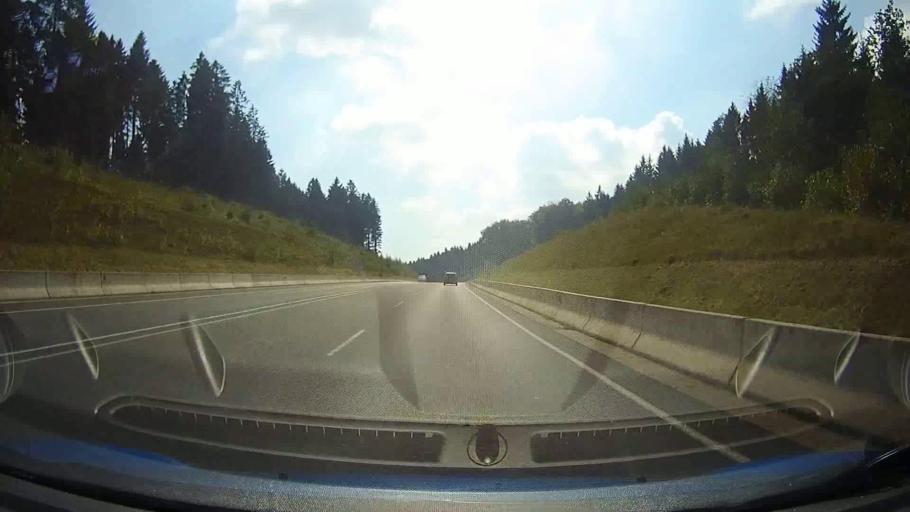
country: DE
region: Lower Saxony
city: Adelebsen
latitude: 51.6419
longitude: 9.7646
